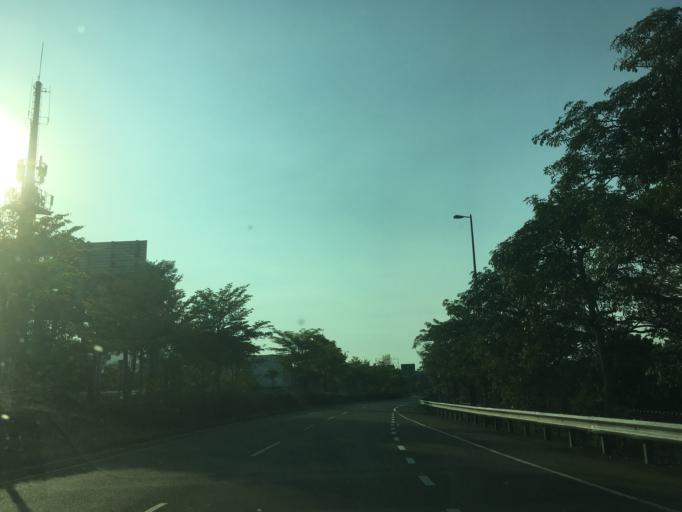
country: TW
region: Taiwan
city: Zhongxing New Village
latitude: 23.9500
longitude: 120.6650
